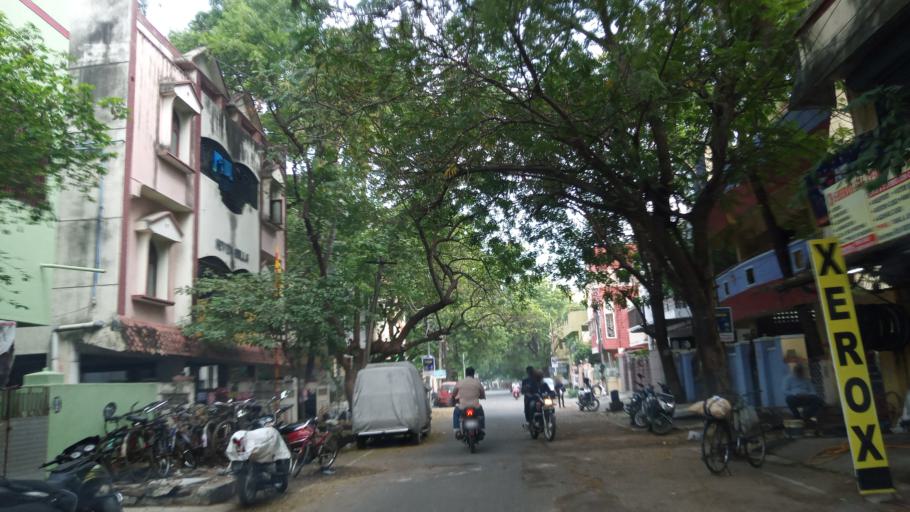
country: IN
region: Tamil Nadu
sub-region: Kancheepuram
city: Alandur
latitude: 13.0388
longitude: 80.2167
